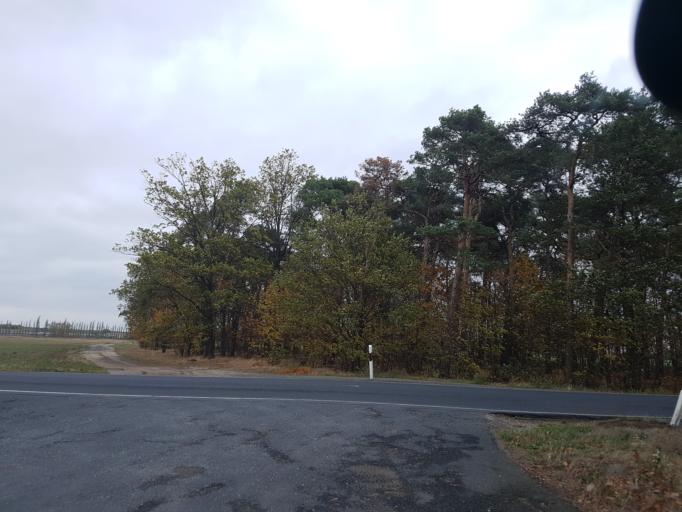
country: DE
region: Saxony-Anhalt
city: Holzdorf
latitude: 51.8309
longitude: 13.1558
